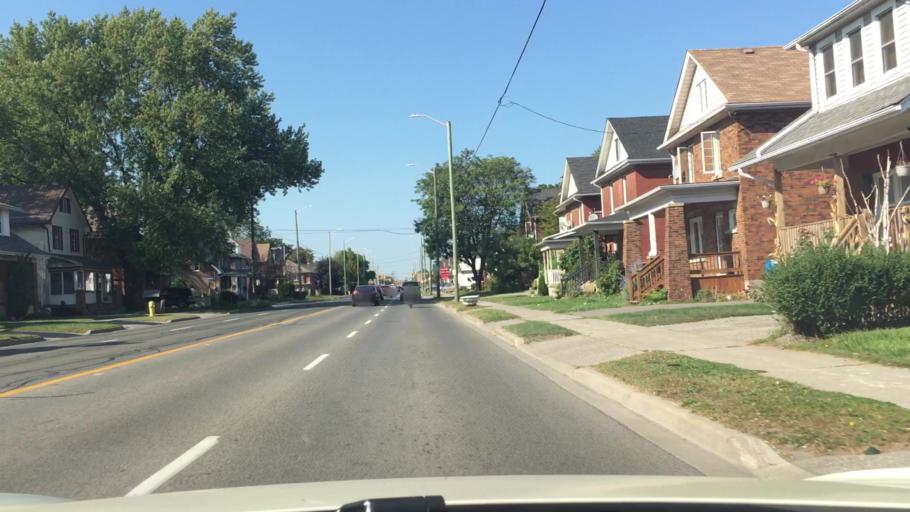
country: CA
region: Ontario
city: Oshawa
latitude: 43.8961
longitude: -78.8521
